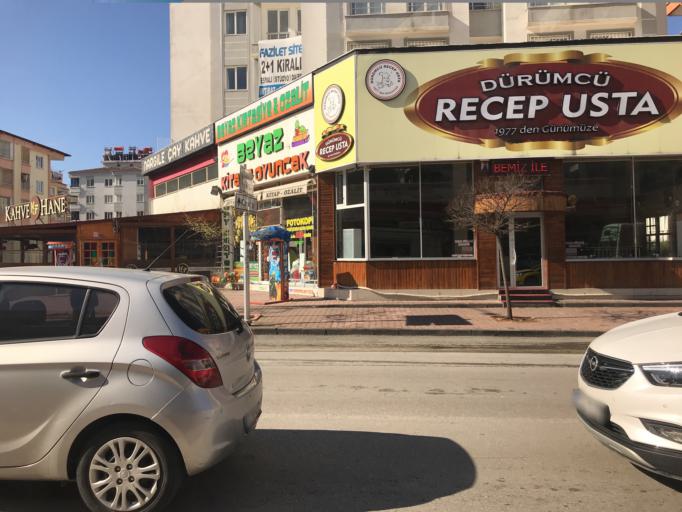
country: TR
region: Gaziantep
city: Sahinbey
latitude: 37.0324
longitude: 37.3218
